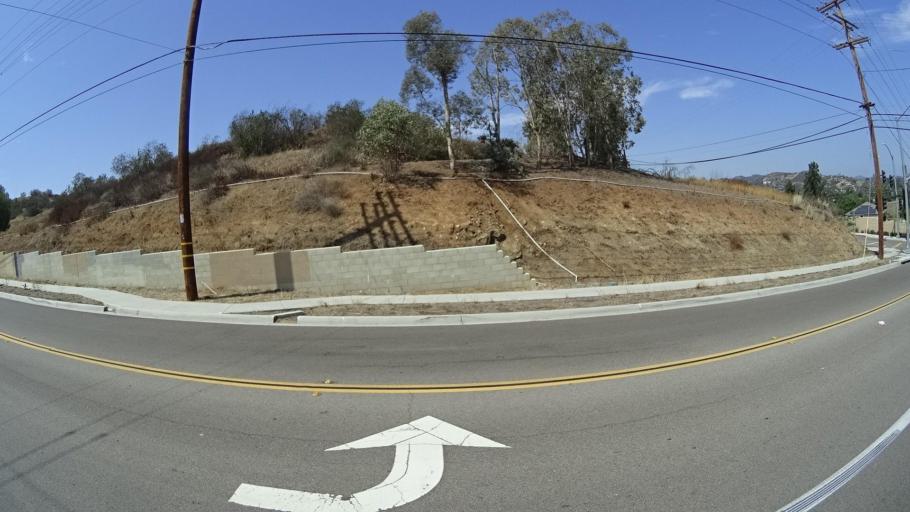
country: US
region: California
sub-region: San Diego County
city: Escondido
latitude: 33.1544
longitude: -117.0831
